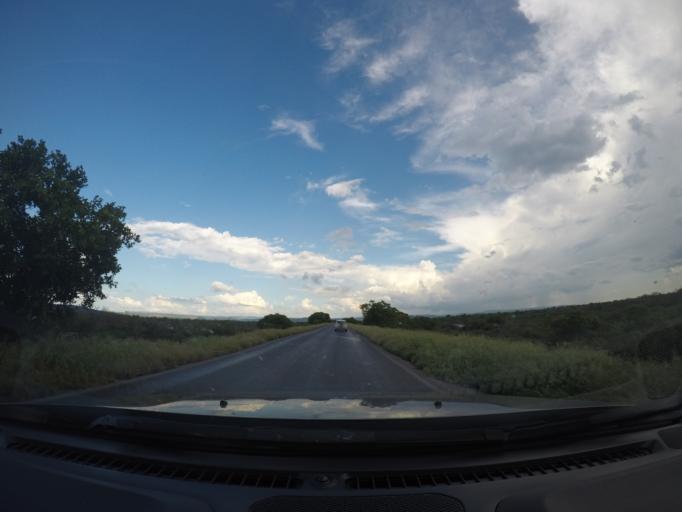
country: BR
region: Bahia
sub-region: Ibotirama
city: Ibotirama
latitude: -12.1571
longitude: -43.3006
